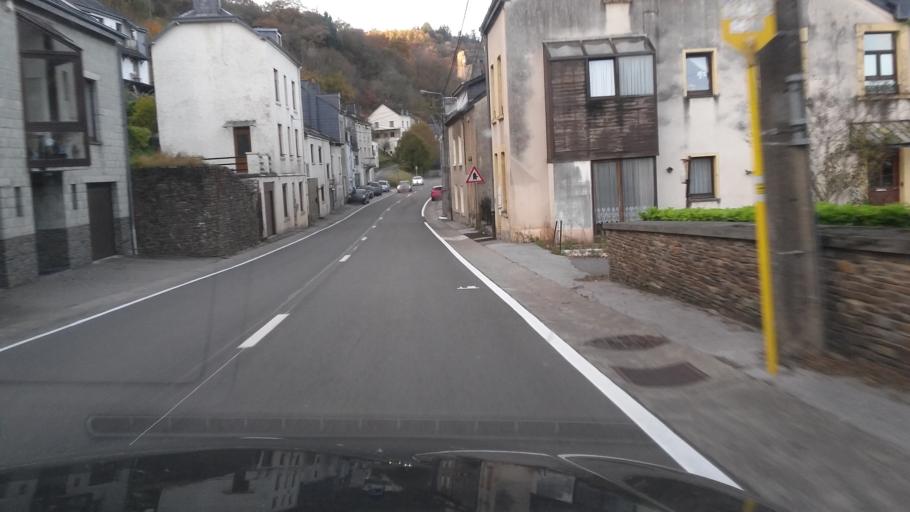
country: BE
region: Wallonia
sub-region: Province du Luxembourg
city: Bouillon
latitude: 49.7883
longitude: 5.0652
